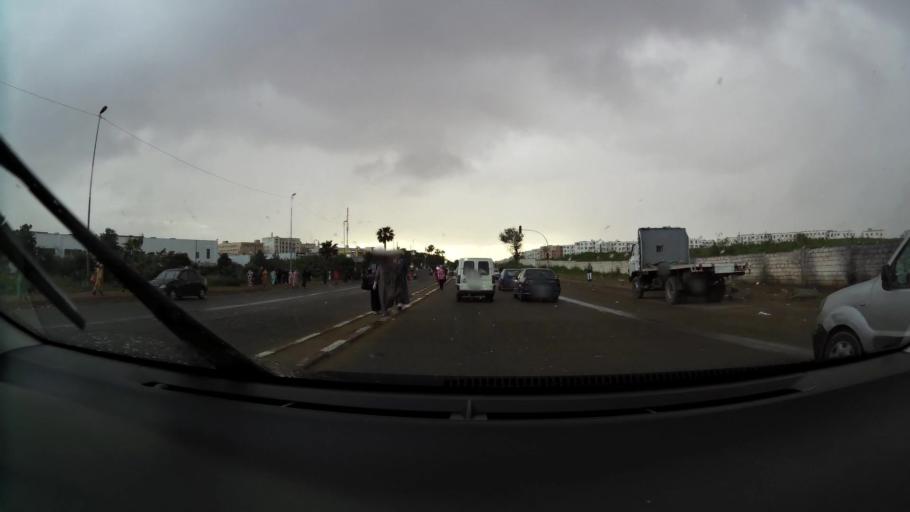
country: MA
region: Grand Casablanca
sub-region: Mediouna
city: Tit Mellil
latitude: 33.5694
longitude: -7.5181
